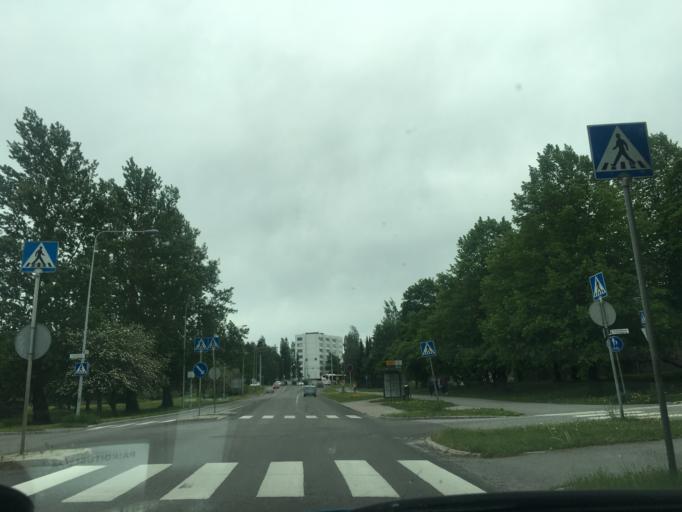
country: FI
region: Varsinais-Suomi
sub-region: Turku
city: Turku
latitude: 60.4602
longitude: 22.3068
